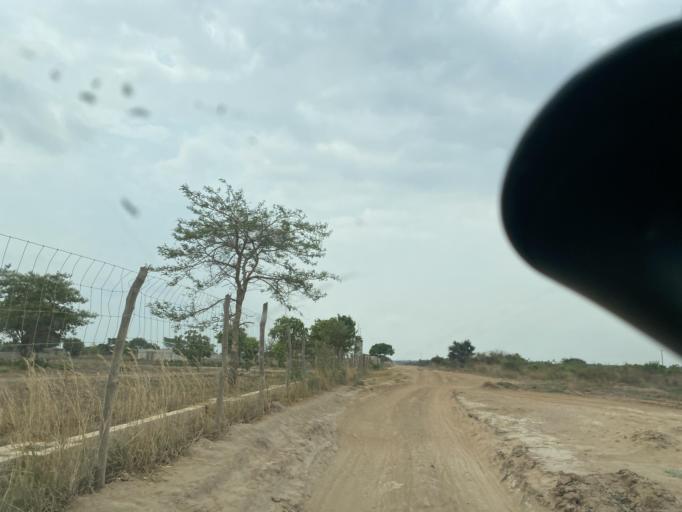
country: ZM
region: Lusaka
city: Lusaka
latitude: -15.2160
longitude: 28.3383
